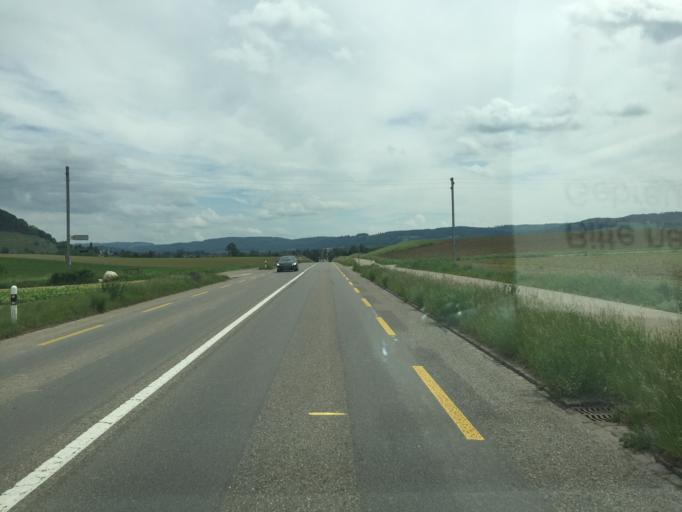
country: CH
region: Thurgau
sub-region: Frauenfeld District
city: Wagenhausen
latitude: 47.6658
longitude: 8.8293
